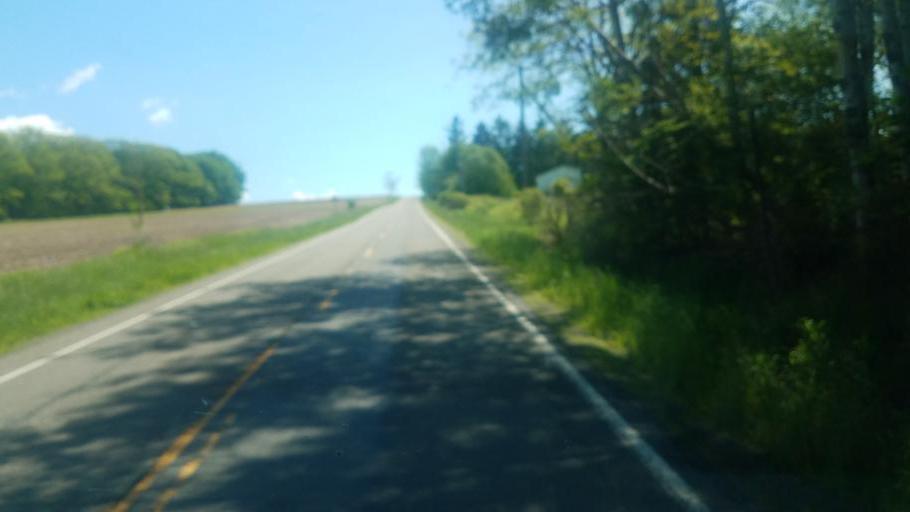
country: US
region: Pennsylvania
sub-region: Tioga County
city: Wellsboro
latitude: 41.7332
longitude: -77.3696
